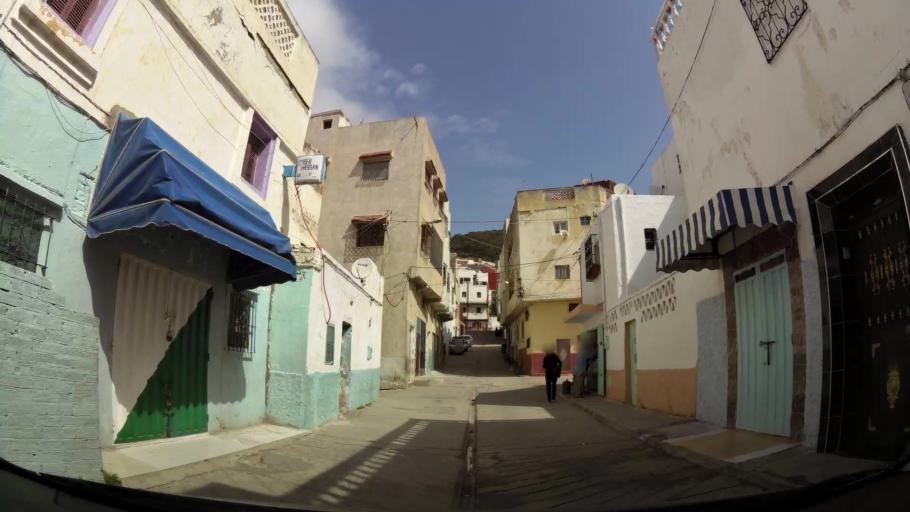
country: MA
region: Tanger-Tetouan
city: Tetouan
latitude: 35.5781
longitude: -5.3876
